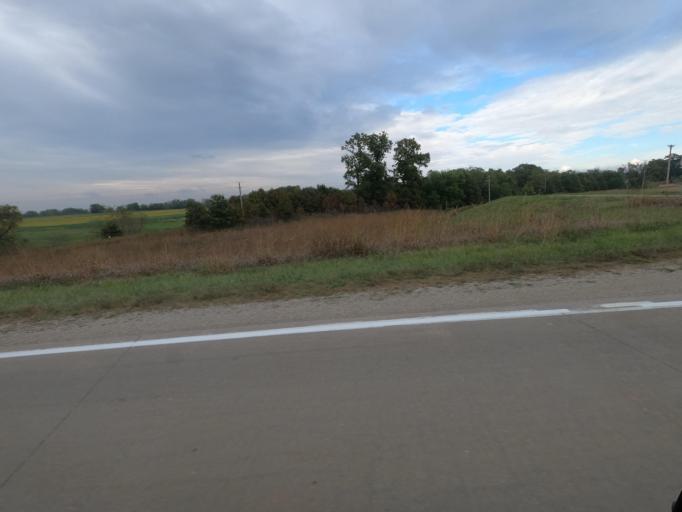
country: US
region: Iowa
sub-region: Henry County
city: Mount Pleasant
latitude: 40.8130
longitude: -91.7053
